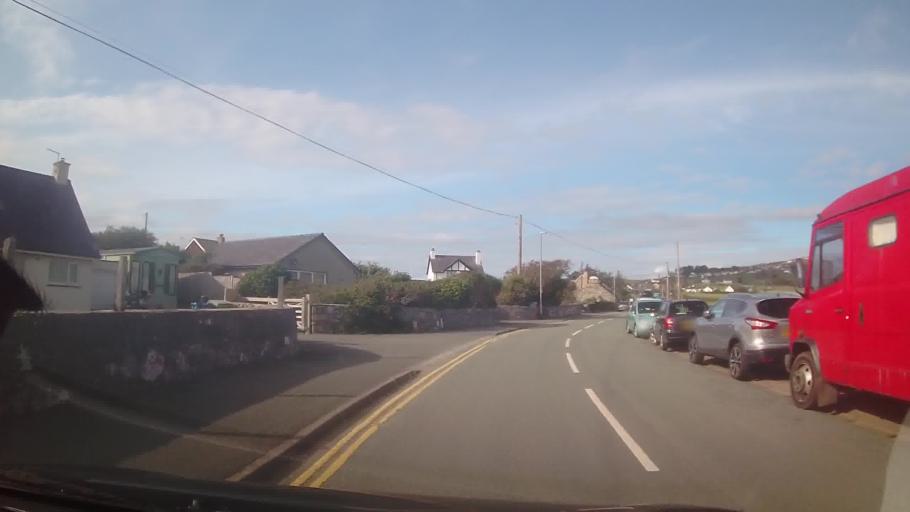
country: GB
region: Wales
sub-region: Gwynedd
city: Llanfair
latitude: 52.8342
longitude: -4.1248
